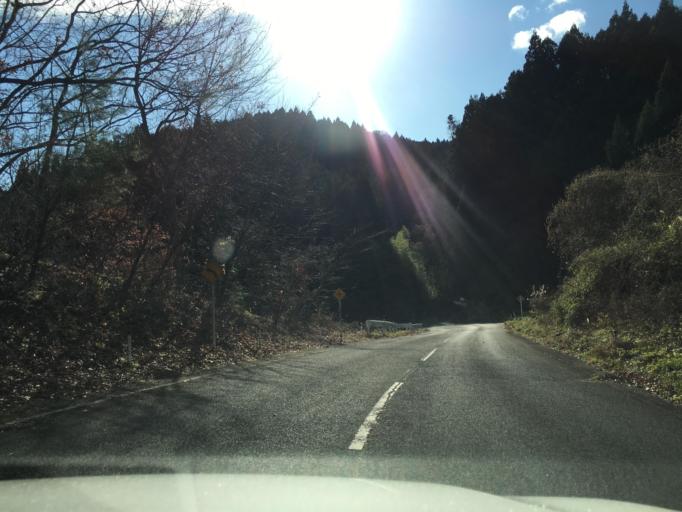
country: JP
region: Fukushima
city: Nihommatsu
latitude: 37.6350
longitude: 140.5906
